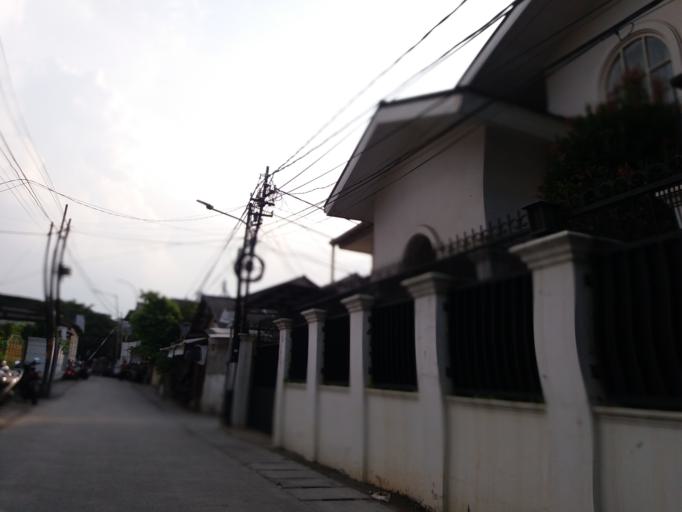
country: ID
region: Jakarta Raya
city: Jakarta
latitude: -6.2465
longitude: 106.8081
